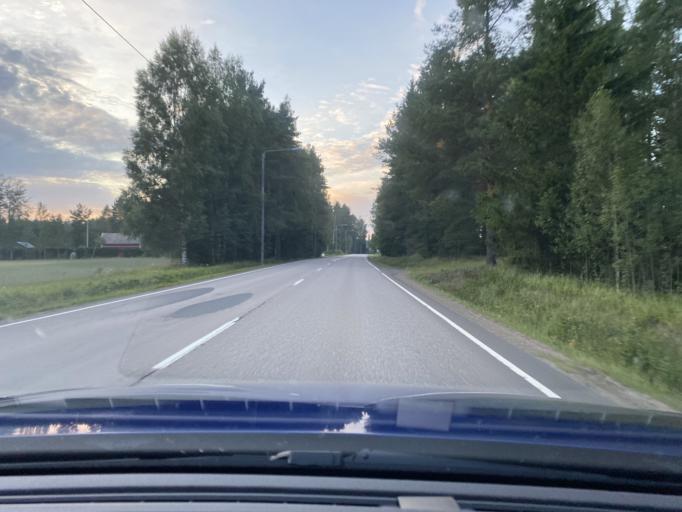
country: FI
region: Satakunta
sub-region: Pohjois-Satakunta
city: Honkajoki
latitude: 61.9604
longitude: 22.2223
